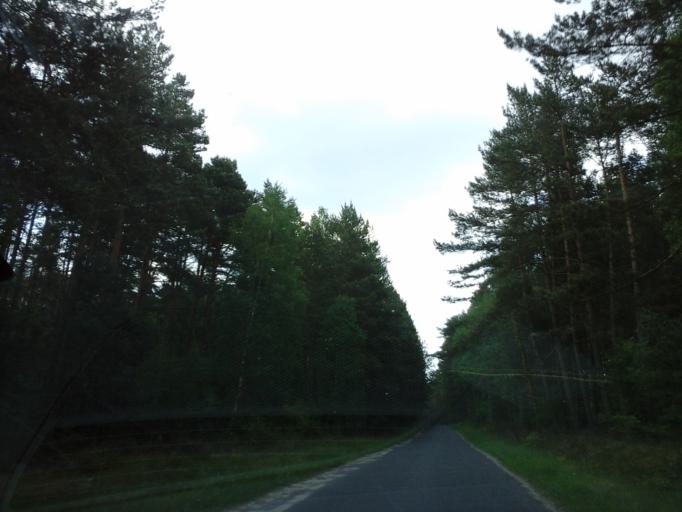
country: PL
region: West Pomeranian Voivodeship
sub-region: Powiat drawski
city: Kalisz Pomorski
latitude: 53.2607
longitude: 15.9791
